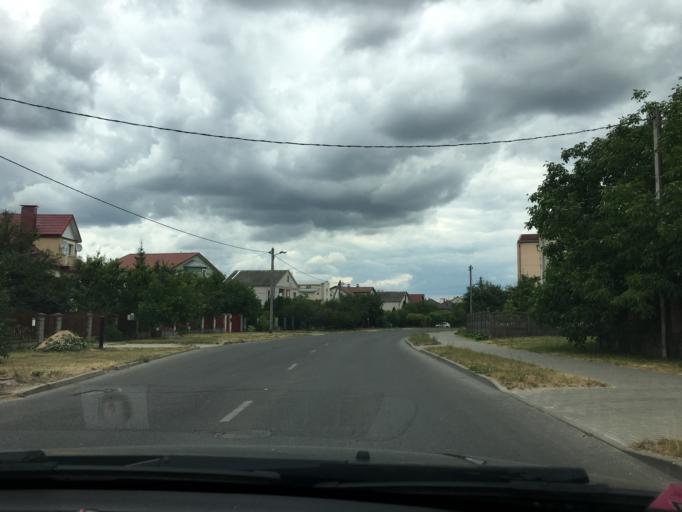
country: BY
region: Grodnenskaya
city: Hrodna
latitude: 53.6237
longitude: 23.8425
